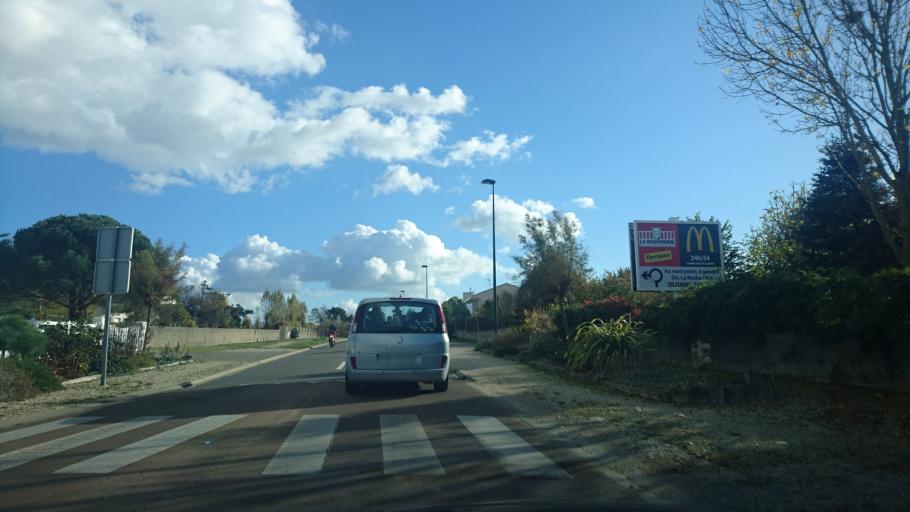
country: FR
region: Pays de la Loire
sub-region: Departement de la Vendee
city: Les Sables-d'Olonne
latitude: 46.5206
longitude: -1.7926
